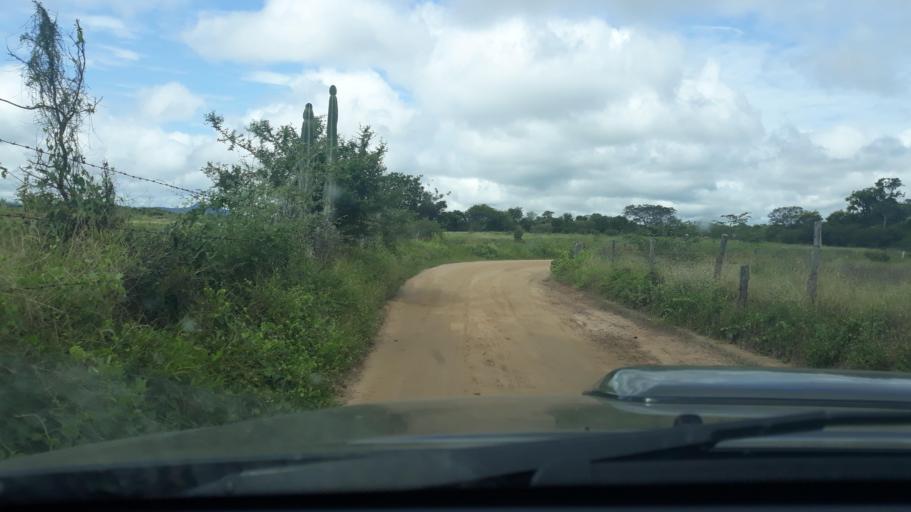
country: BR
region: Bahia
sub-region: Riacho De Santana
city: Riacho de Santana
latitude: -13.9112
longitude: -42.9472
